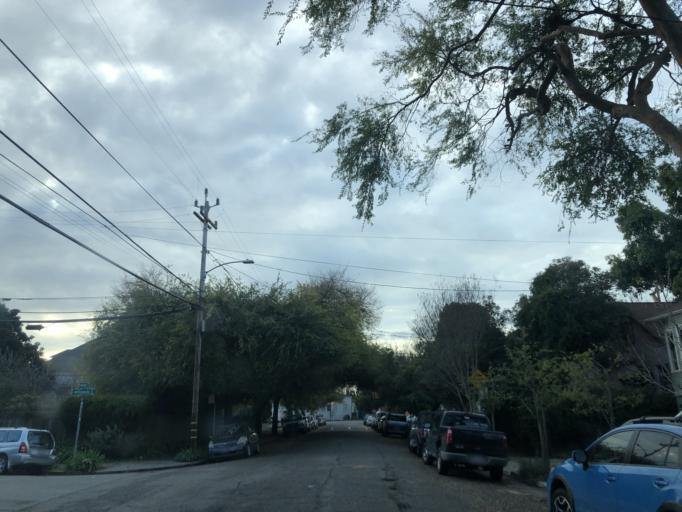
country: US
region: California
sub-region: Alameda County
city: Emeryville
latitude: 37.8445
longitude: -122.2598
